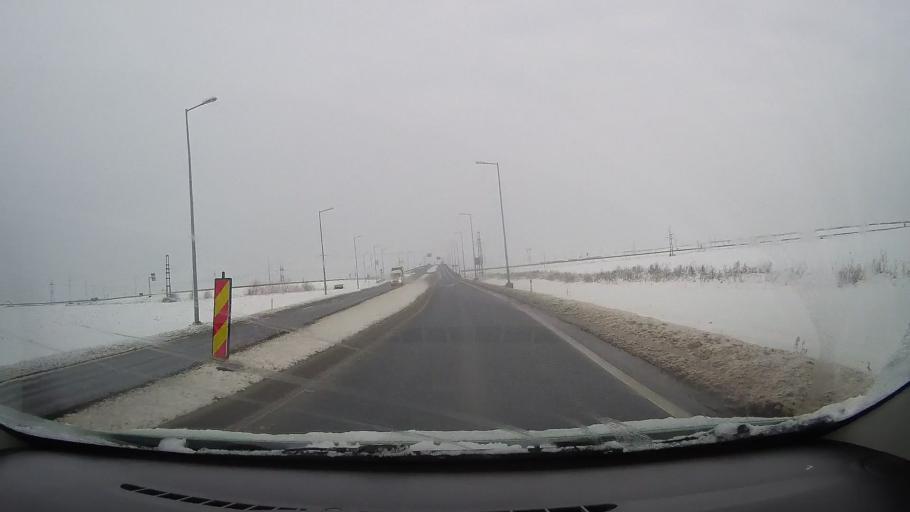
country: RO
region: Alba
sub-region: Municipiul Sebes
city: Lancram
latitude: 45.9737
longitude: 23.5243
